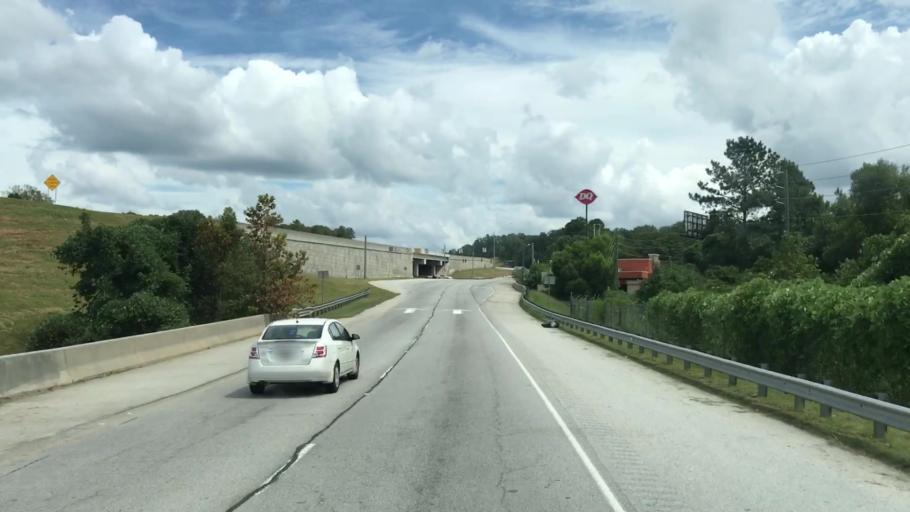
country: US
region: Georgia
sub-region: DeKalb County
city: Lithonia
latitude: 33.7011
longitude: -84.1196
